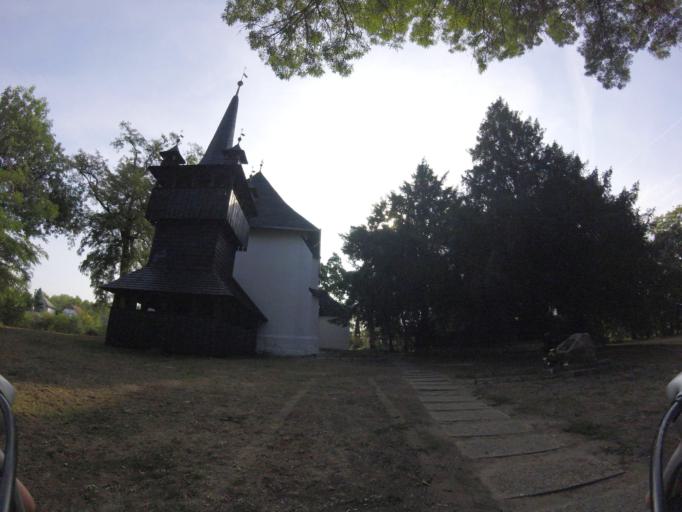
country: HU
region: Szabolcs-Szatmar-Bereg
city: Porcsalma
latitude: 47.9634
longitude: 22.6076
